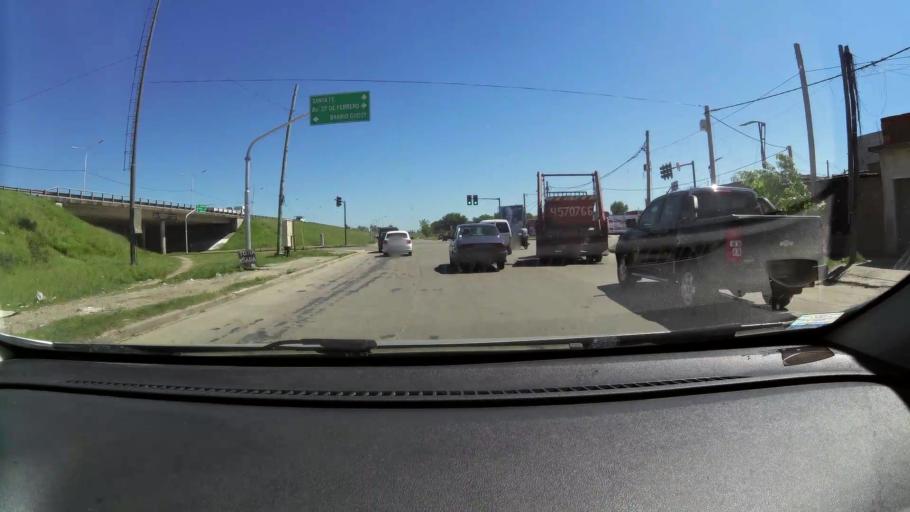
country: AR
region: Santa Fe
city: Perez
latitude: -32.9599
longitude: -60.7203
